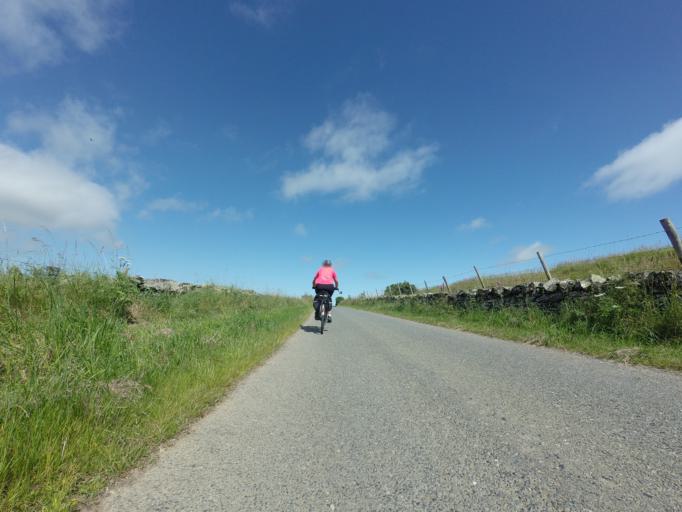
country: GB
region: Scotland
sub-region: Aberdeenshire
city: Banff
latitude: 57.6008
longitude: -2.5115
